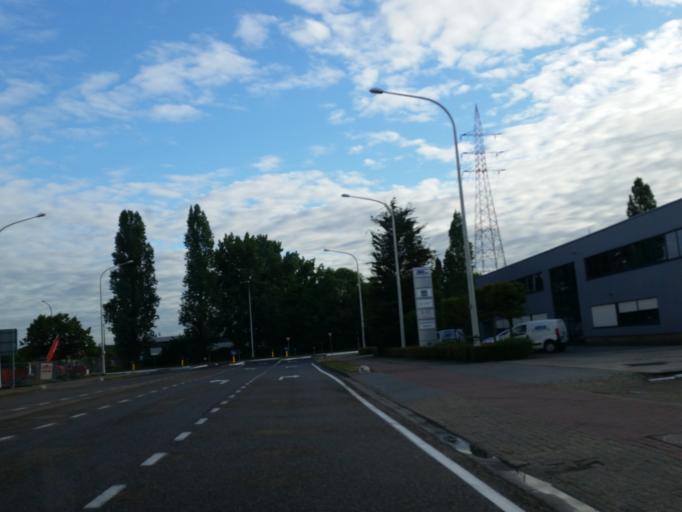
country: BE
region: Flanders
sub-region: Provincie Antwerpen
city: Antwerpen
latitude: 51.2724
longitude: 4.4008
